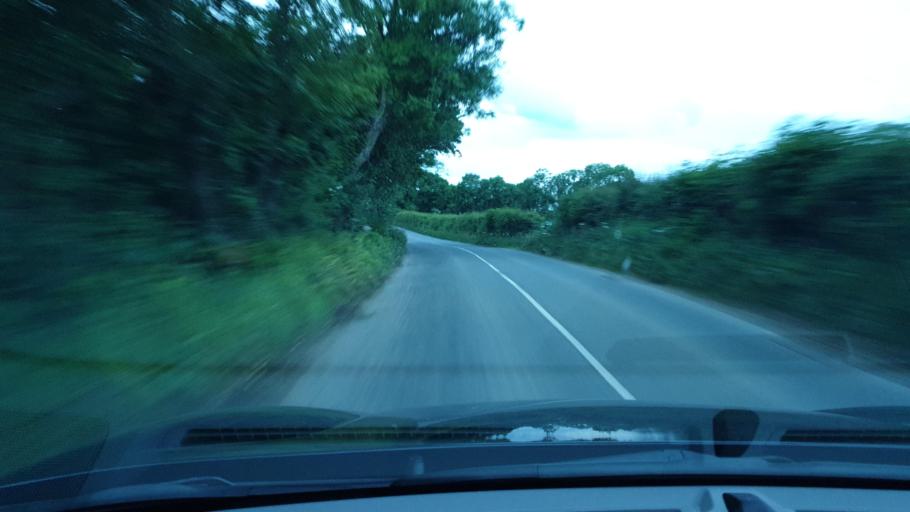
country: IE
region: Leinster
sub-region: An Mhi
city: Ashbourne
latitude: 53.5674
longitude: -6.4245
